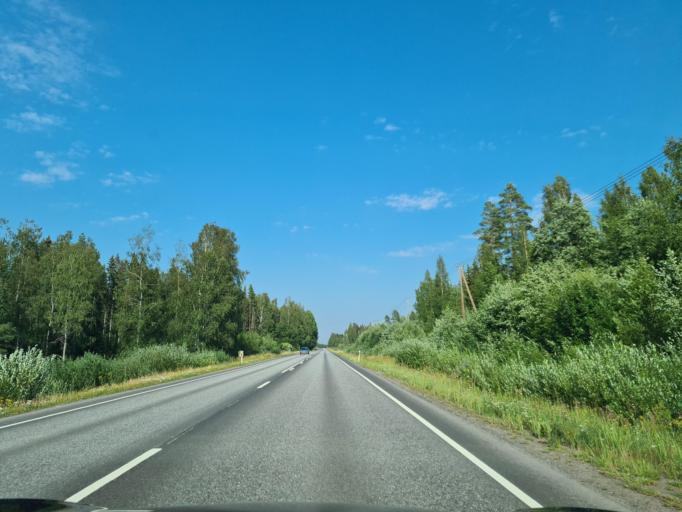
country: FI
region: Satakunta
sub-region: Pori
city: Laengelmaeki
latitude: 61.7755
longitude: 22.1874
